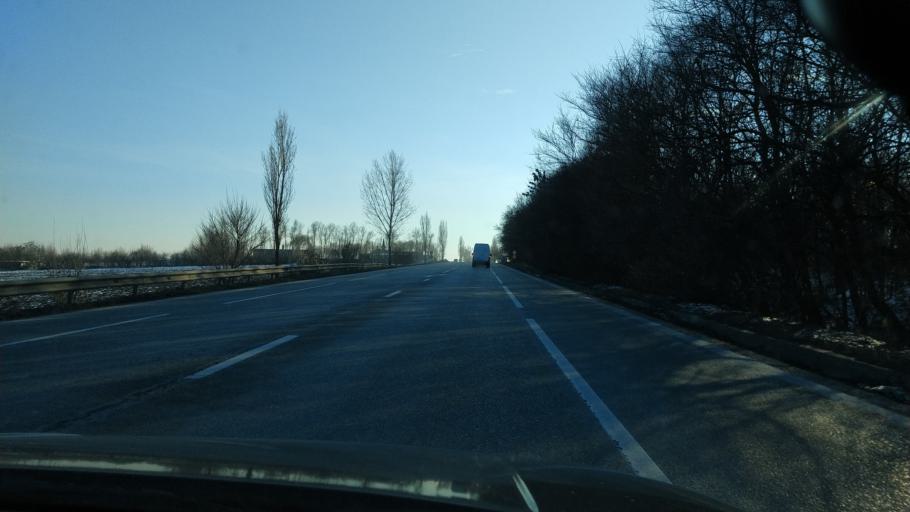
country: RO
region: Bacau
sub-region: Comuna Filipesti
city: Filipesti
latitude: 46.7045
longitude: 26.8918
